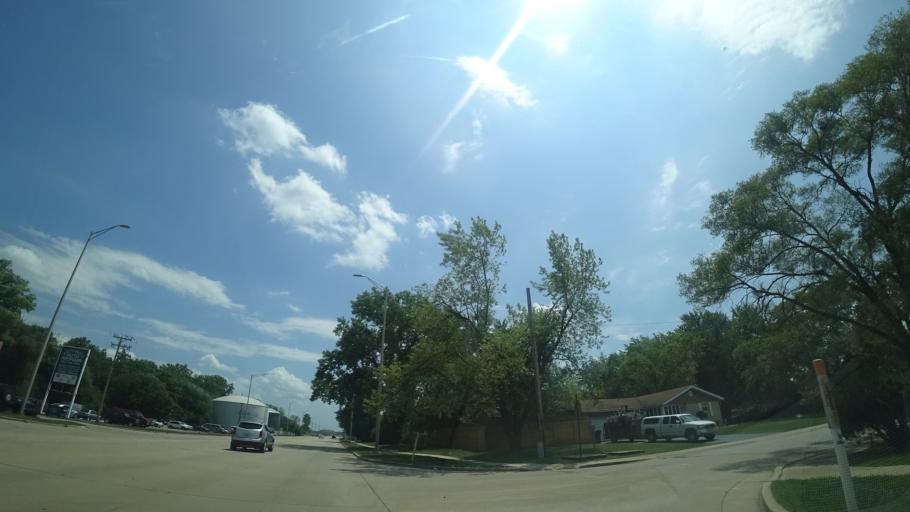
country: US
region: Illinois
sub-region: Cook County
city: Crestwood
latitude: 41.6602
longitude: -87.7509
